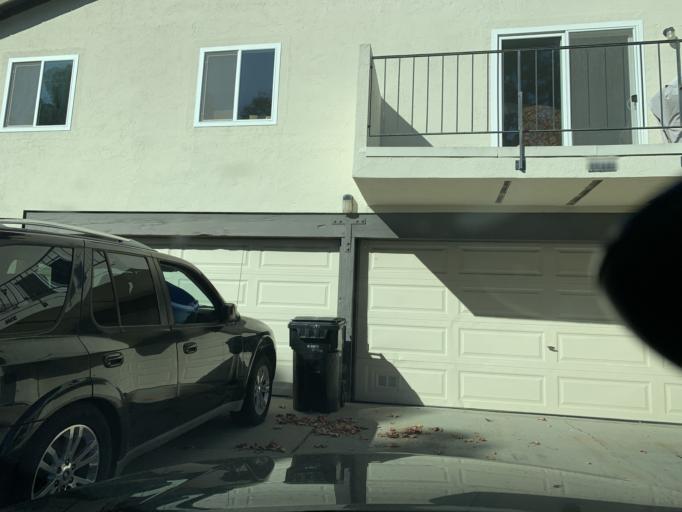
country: US
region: California
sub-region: San Diego County
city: Poway
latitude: 32.9655
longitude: -117.0984
